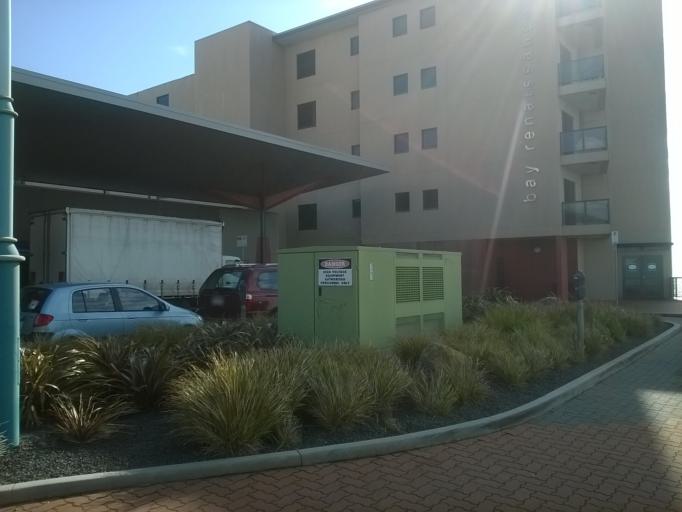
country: AU
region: Tasmania
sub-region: Burnie
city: Burnie
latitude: -41.0507
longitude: 145.9084
